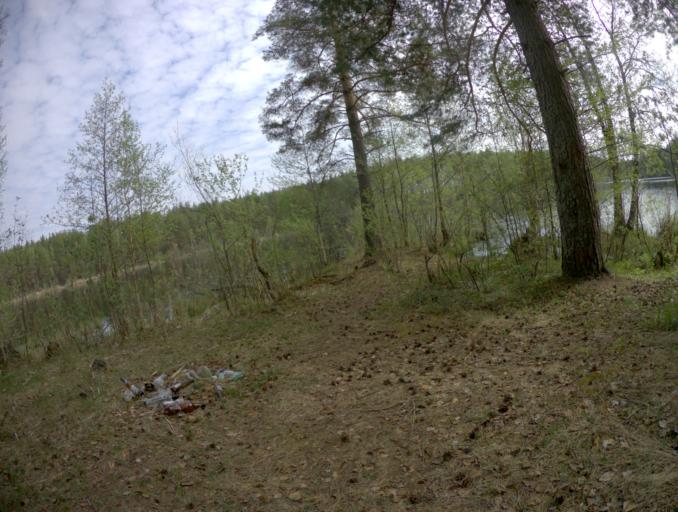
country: RU
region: Ivanovo
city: Talitsy
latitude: 56.4838
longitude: 42.1625
